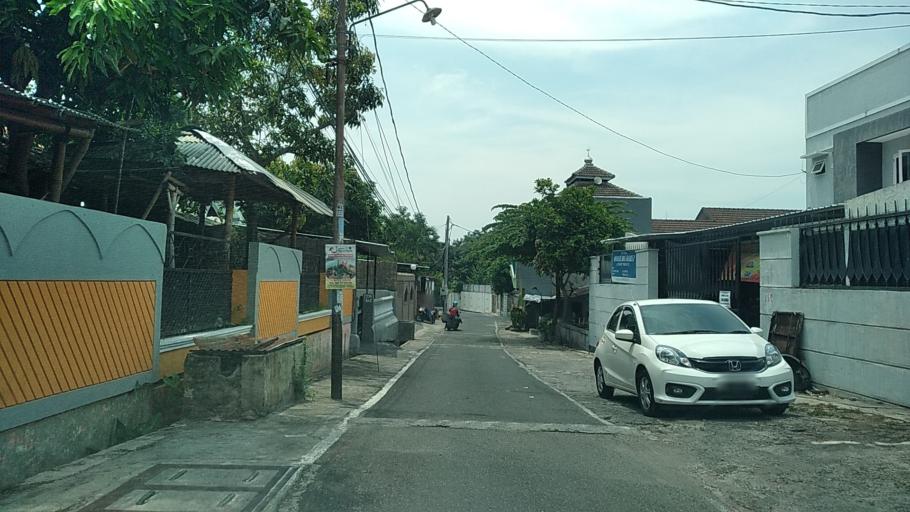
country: ID
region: Central Java
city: Semarang
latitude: -7.0457
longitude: 110.4225
